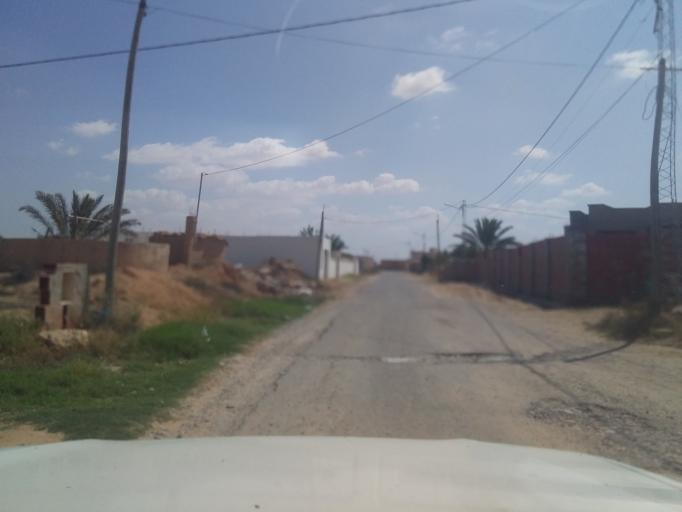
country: TN
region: Madanin
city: Medenine
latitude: 33.6128
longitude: 10.3006
